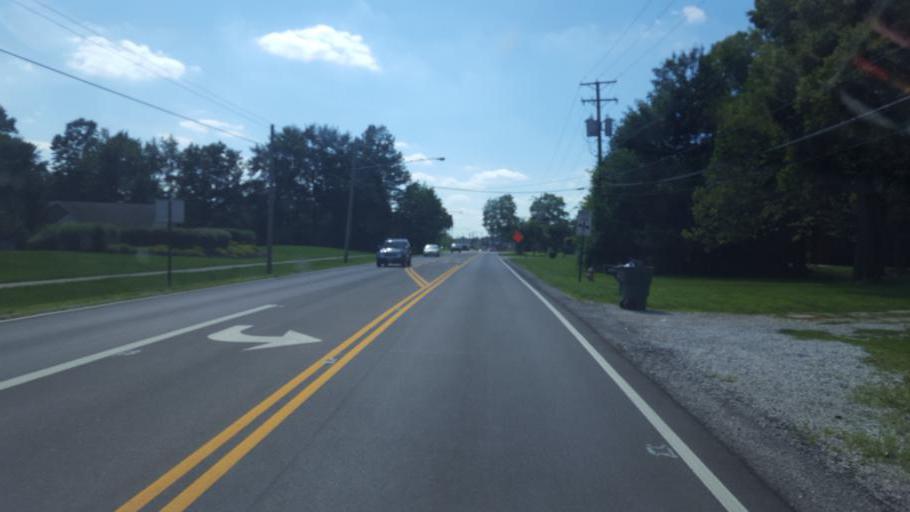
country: US
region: Ohio
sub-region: Franklin County
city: Minerva Park
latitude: 40.0371
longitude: -82.9483
